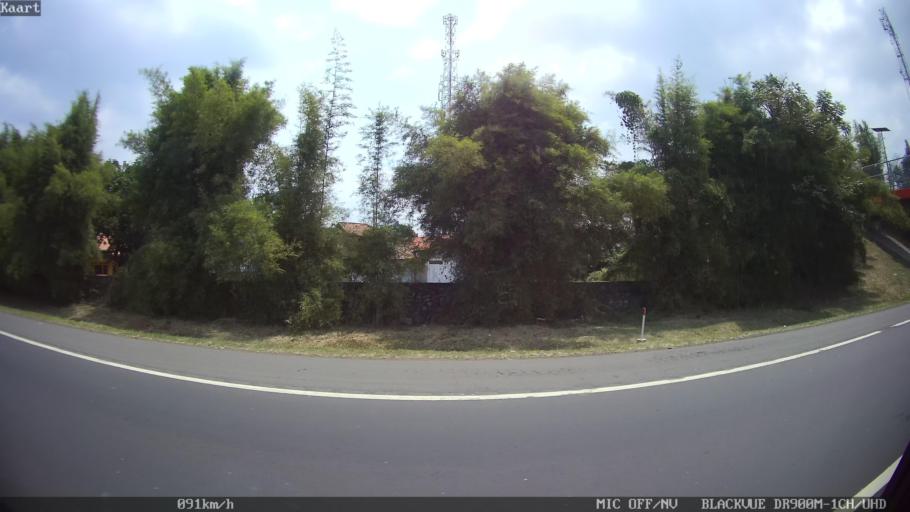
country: ID
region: Banten
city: Bojonegara
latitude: -6.0347
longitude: 106.1015
